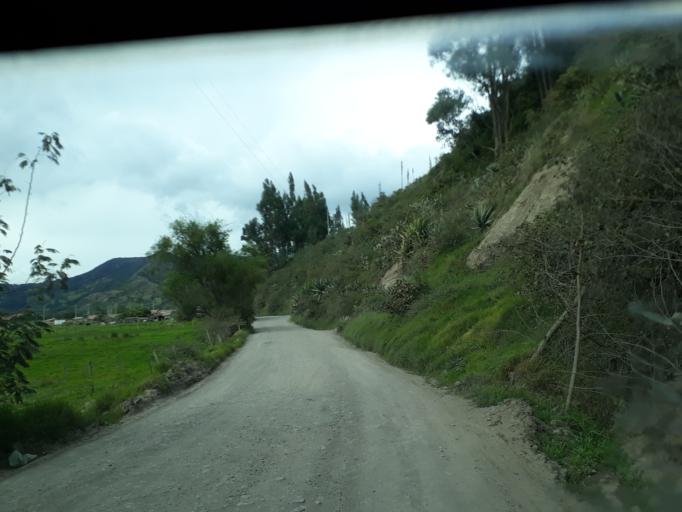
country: CO
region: Cundinamarca
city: Cucunuba
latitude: 5.2505
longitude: -73.7847
